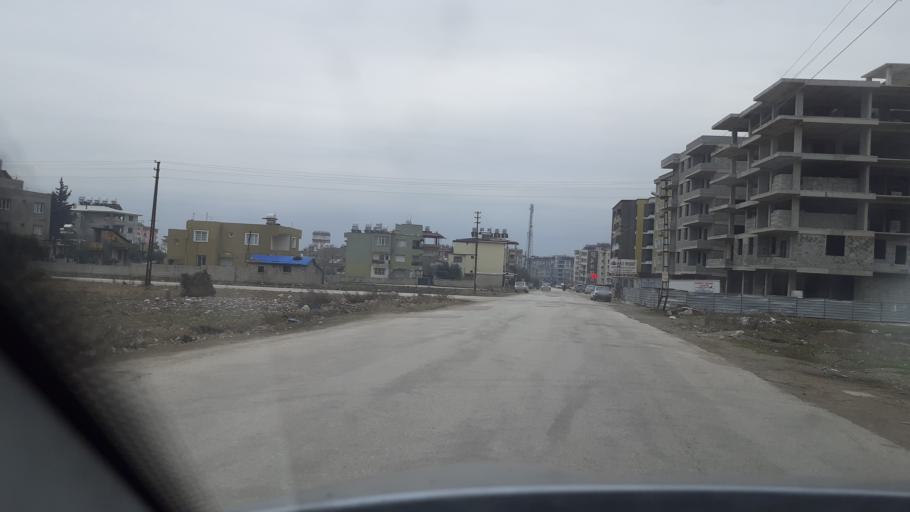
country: TR
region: Hatay
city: Kirikhan
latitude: 36.4859
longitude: 36.3556
